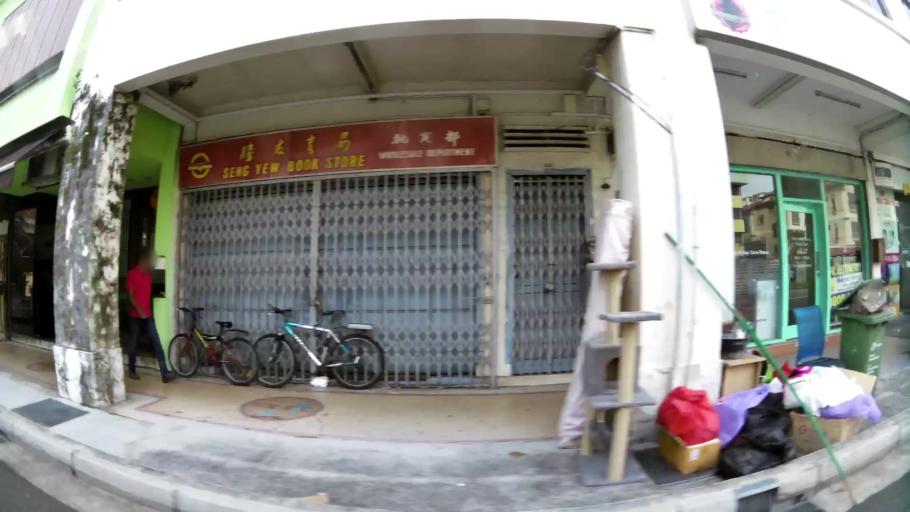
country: SG
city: Singapore
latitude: 1.3120
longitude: 103.9050
